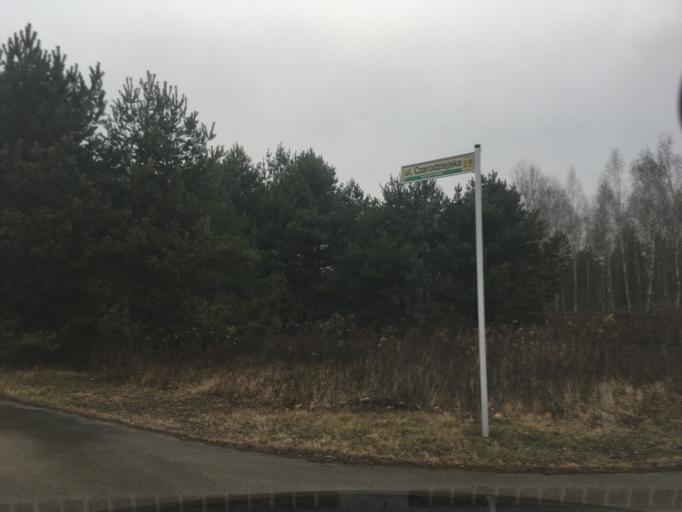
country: PL
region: Masovian Voivodeship
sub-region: Powiat piaseczynski
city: Lesznowola
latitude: 52.0751
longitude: 20.9252
